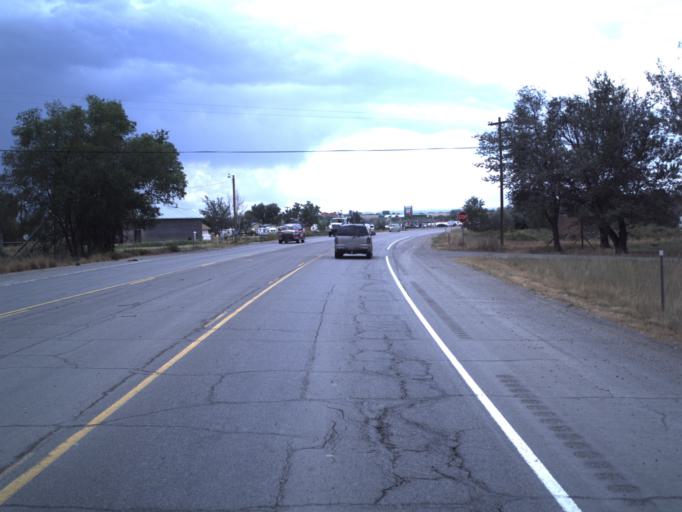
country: US
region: Utah
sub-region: Duchesne County
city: Roosevelt
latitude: 40.1967
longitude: -110.0697
